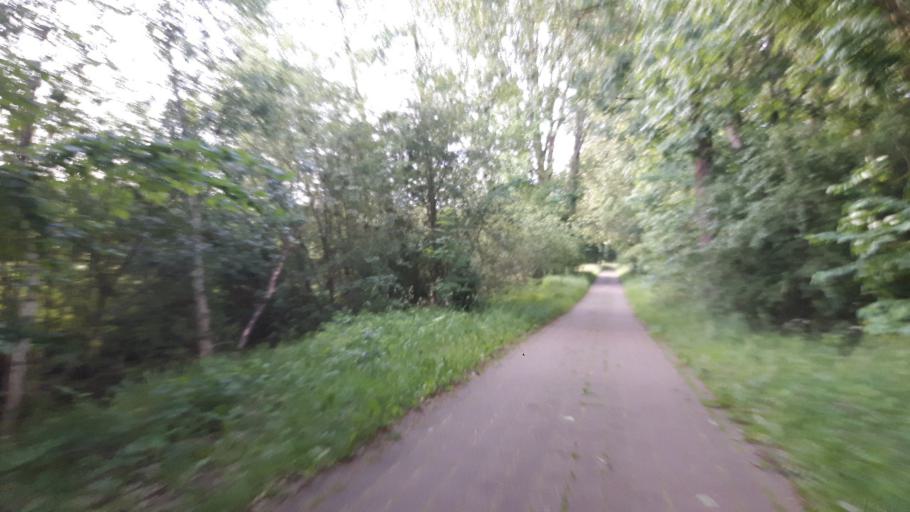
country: DE
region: Brandenburg
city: Gartz
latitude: 53.2213
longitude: 14.4064
